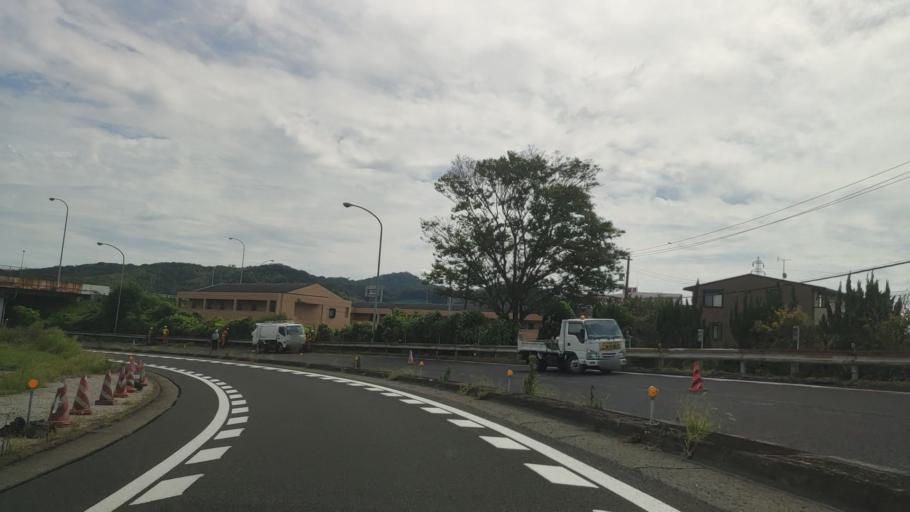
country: JP
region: Wakayama
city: Wakayama-shi
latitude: 34.2402
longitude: 135.2121
